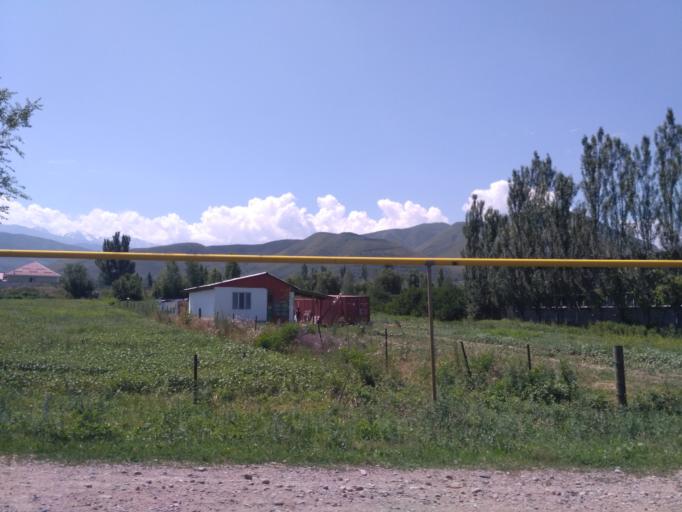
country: KZ
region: Almaty Oblysy
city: Burunday
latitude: 43.1664
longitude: 76.5968
